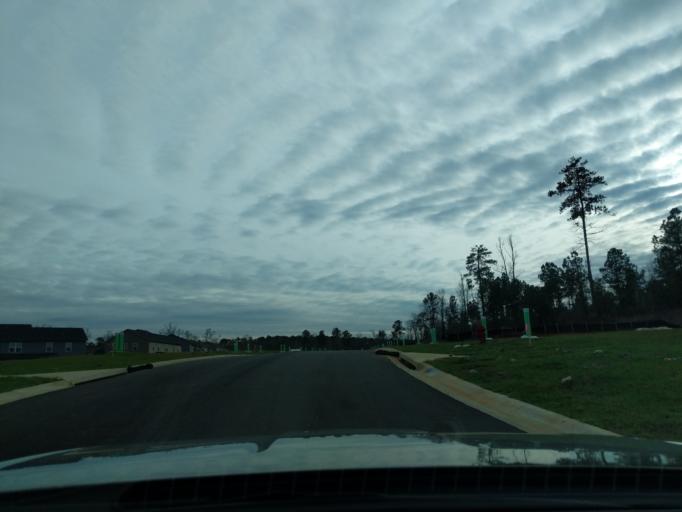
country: US
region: Georgia
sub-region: Columbia County
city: Grovetown
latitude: 33.4678
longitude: -82.2035
